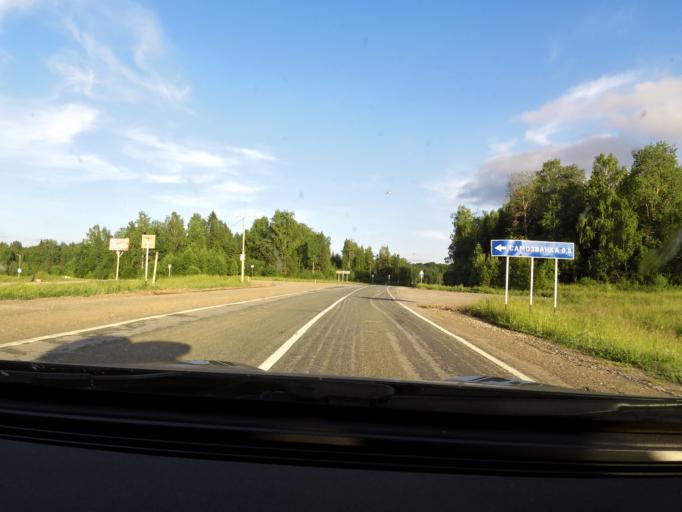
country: RU
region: Perm
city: Siva
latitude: 58.6277
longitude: 53.8688
